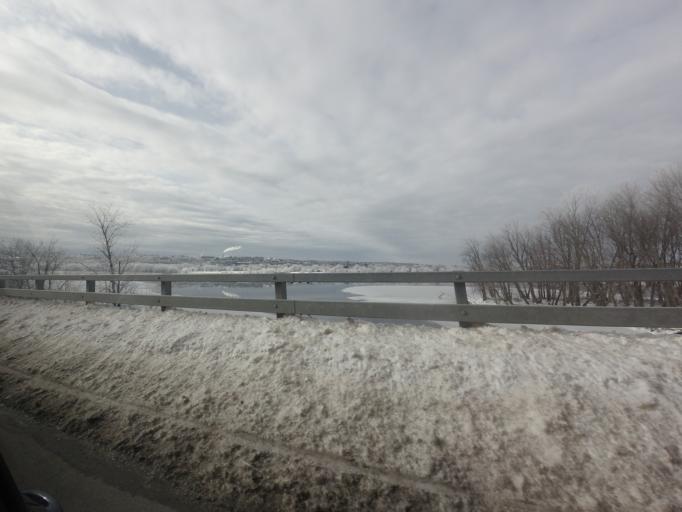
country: CA
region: New Brunswick
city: Fredericton
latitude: 45.9547
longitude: -66.6231
